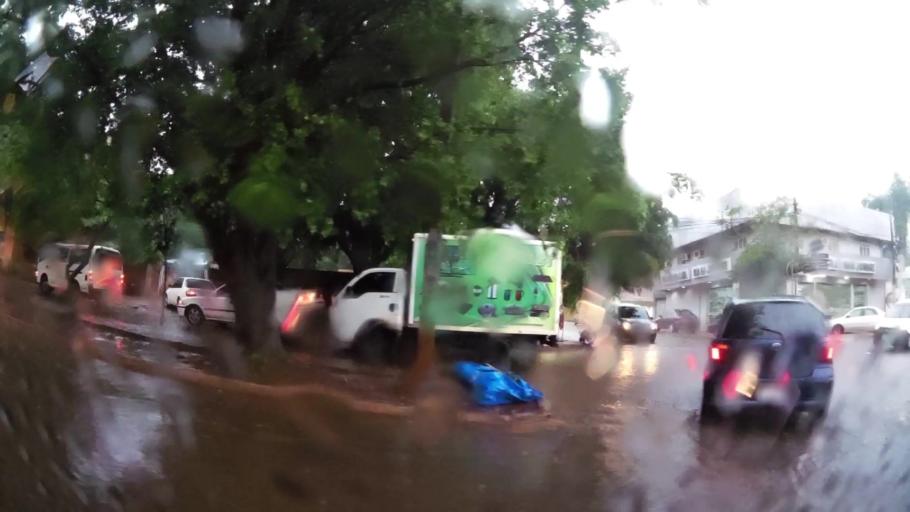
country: PY
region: Alto Parana
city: Ciudad del Este
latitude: -25.4987
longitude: -54.6665
